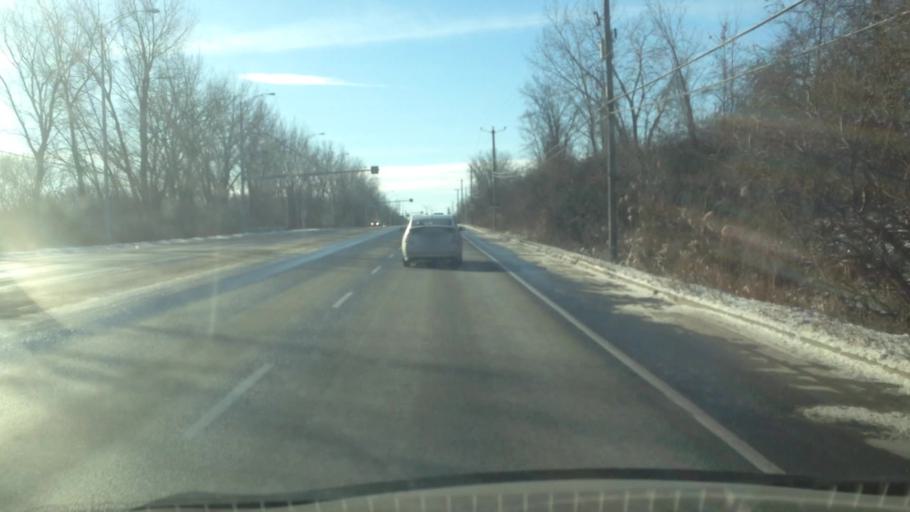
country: CA
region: Quebec
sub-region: Monteregie
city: Chateauguay
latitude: 45.3831
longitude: -73.7016
